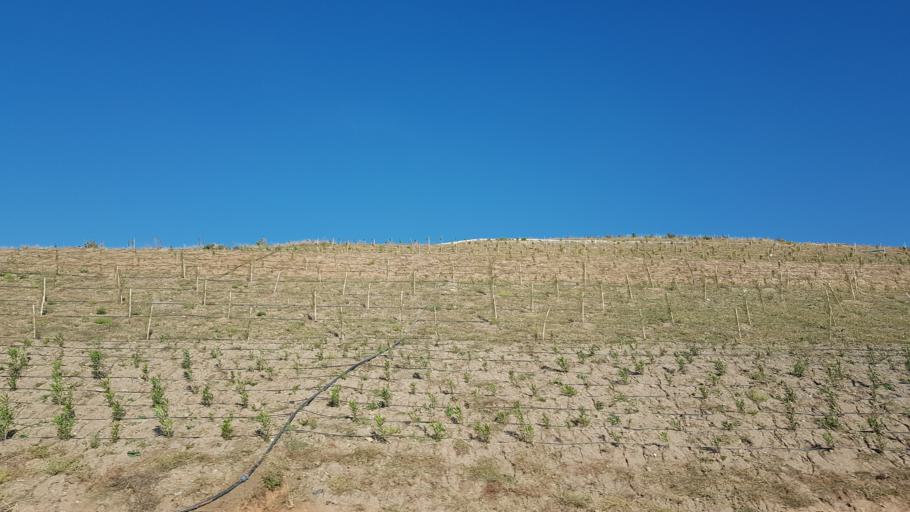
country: TR
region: Balikesir
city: Ertugrul
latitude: 39.5895
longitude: 27.6991
